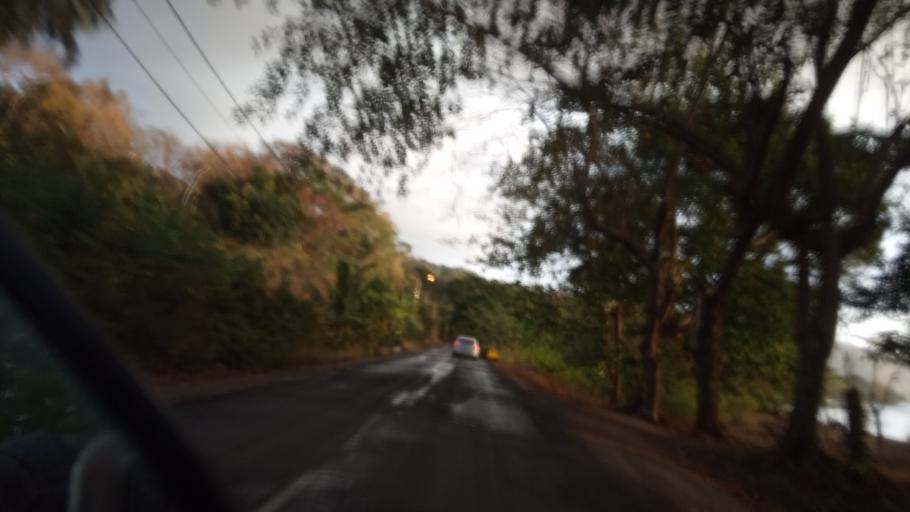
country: YT
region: Kani-Keli
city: Kani Keli
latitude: -12.9311
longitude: 45.1043
